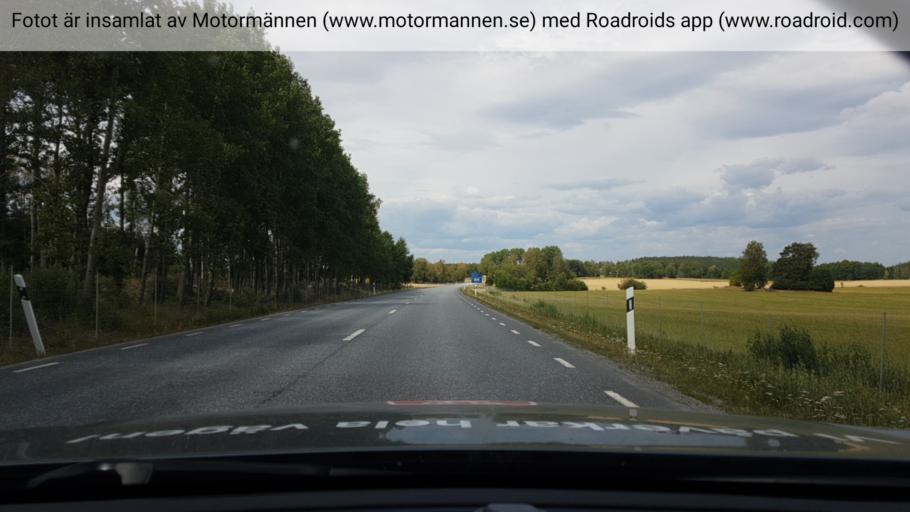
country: SE
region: Stockholm
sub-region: Upplands-Bro Kommun
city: Bro
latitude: 59.5912
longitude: 17.6198
